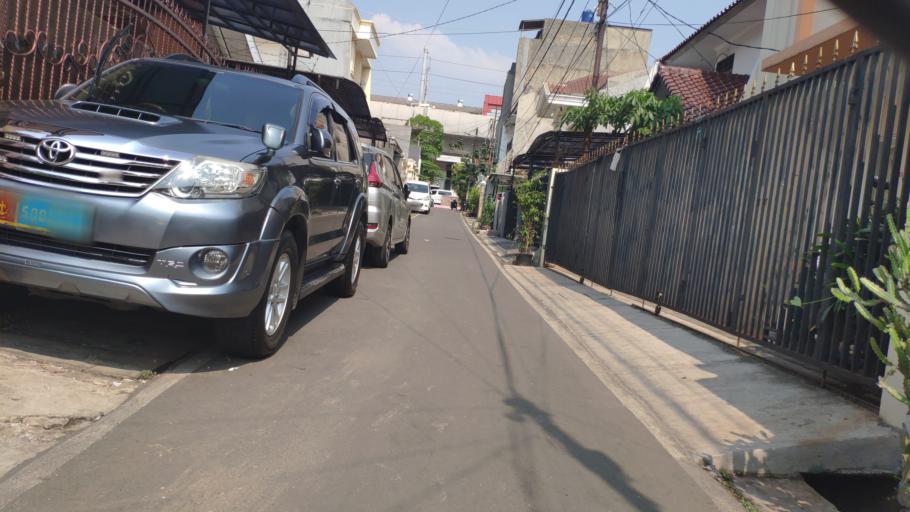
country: ID
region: Jakarta Raya
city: Jakarta
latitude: -6.2501
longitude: 106.7967
